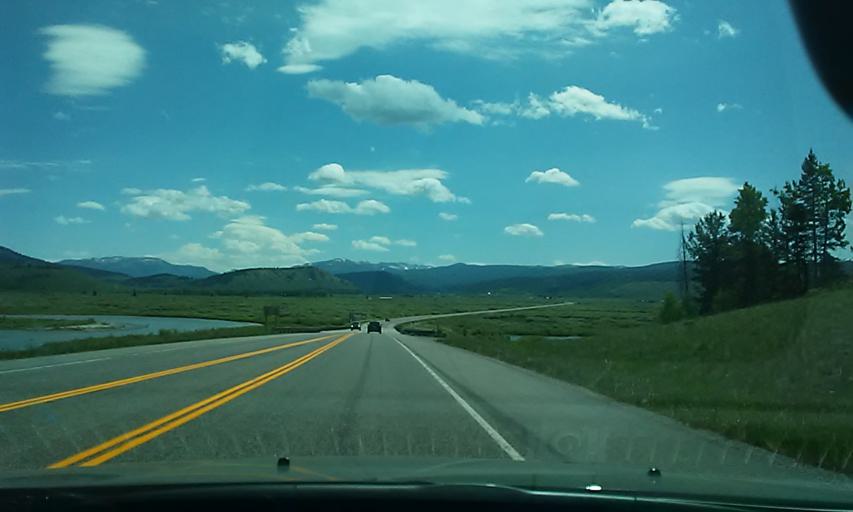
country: US
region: Wyoming
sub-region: Teton County
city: Jackson
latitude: 43.8384
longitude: -110.4428
